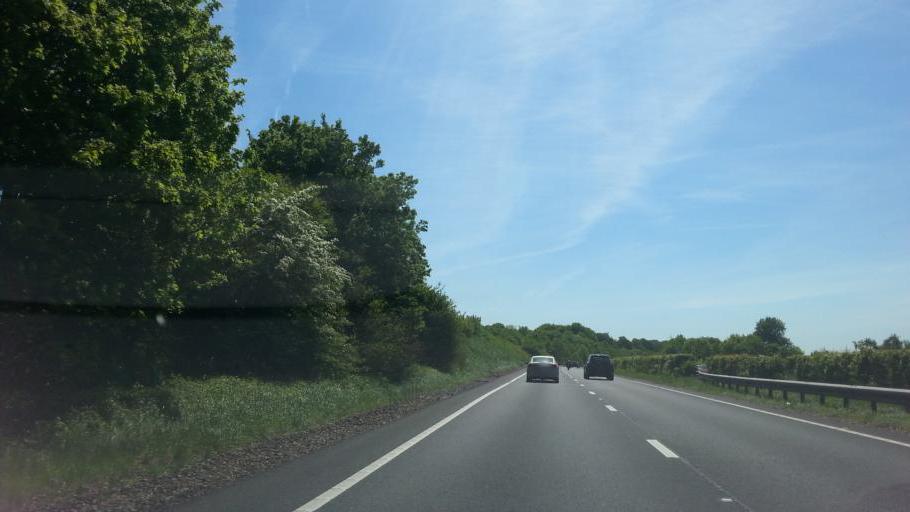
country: GB
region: England
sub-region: Hampshire
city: Overton
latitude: 51.1864
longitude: -1.2735
